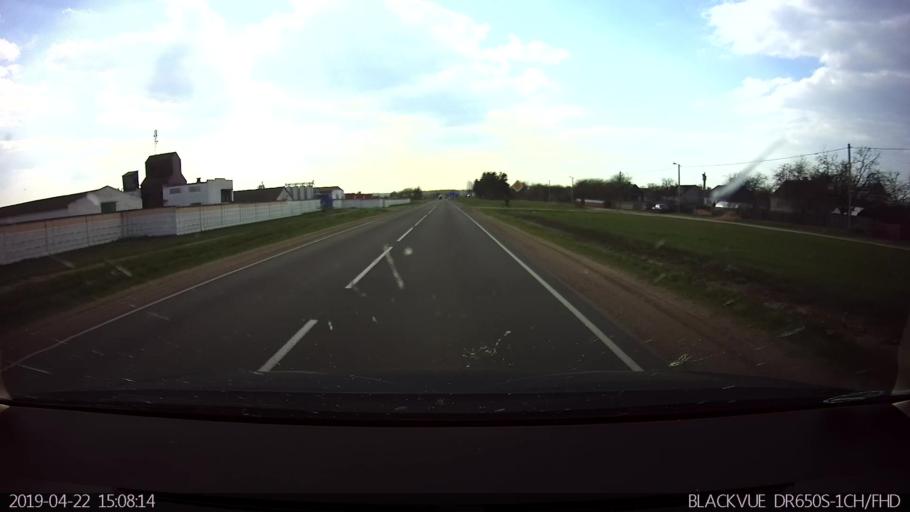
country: BY
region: Brest
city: Kamyanyets
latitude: 52.3272
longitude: 23.7910
